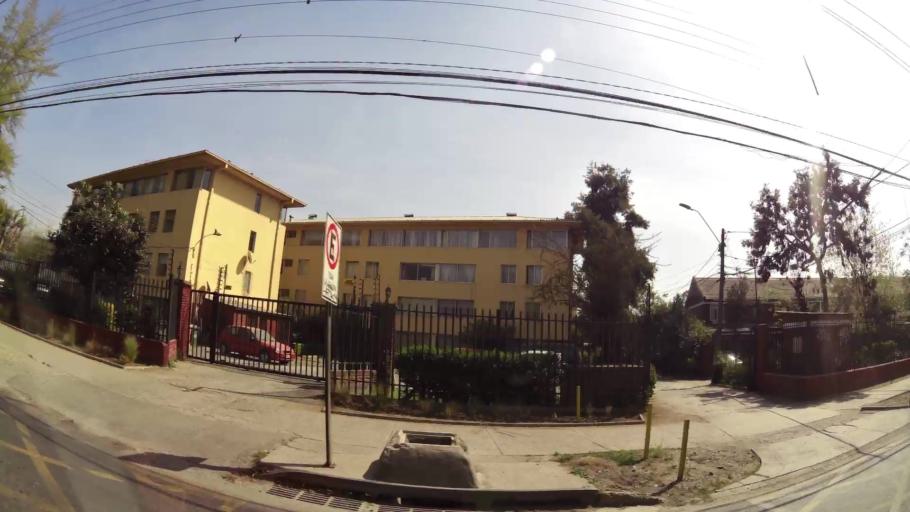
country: CL
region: Santiago Metropolitan
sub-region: Provincia de Santiago
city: Villa Presidente Frei, Nunoa, Santiago, Chile
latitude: -33.5063
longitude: -70.5886
